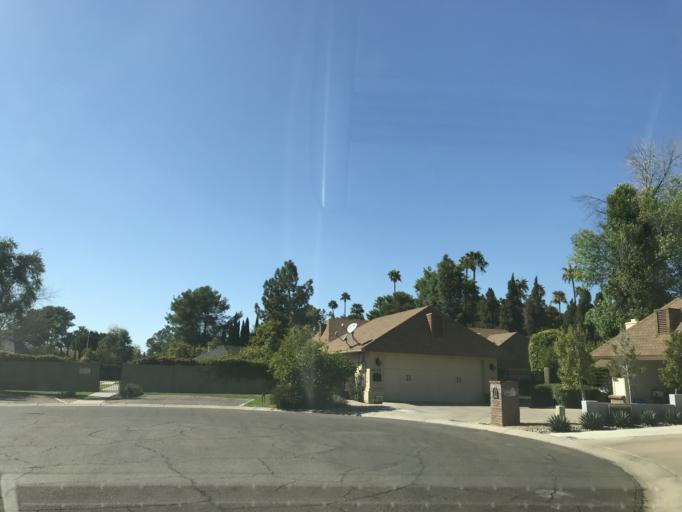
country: US
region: Arizona
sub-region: Maricopa County
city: Phoenix
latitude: 33.5107
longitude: -112.0349
